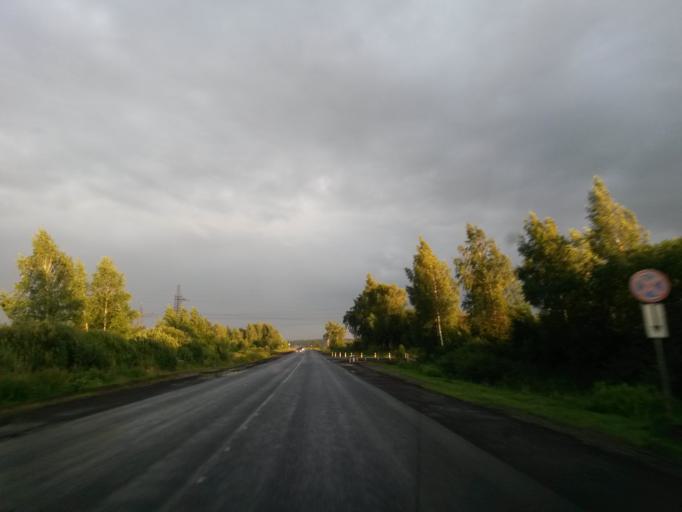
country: RU
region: Jaroslavl
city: Yaroslavl
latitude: 57.5291
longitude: 39.8768
